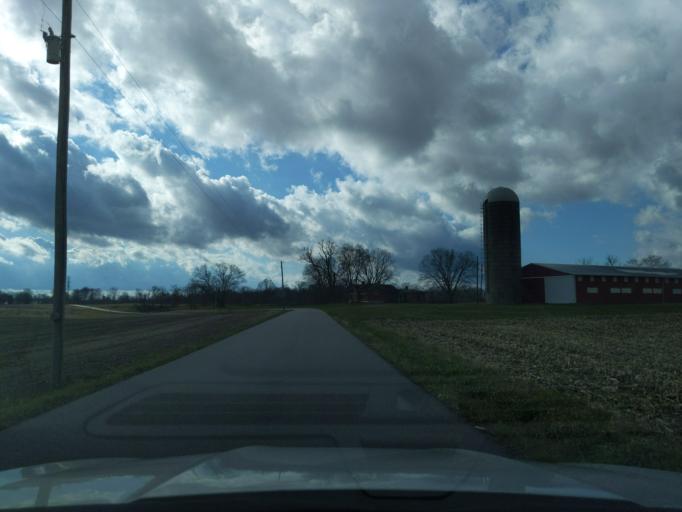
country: US
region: Indiana
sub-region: Decatur County
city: Greensburg
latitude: 39.4004
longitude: -85.5090
